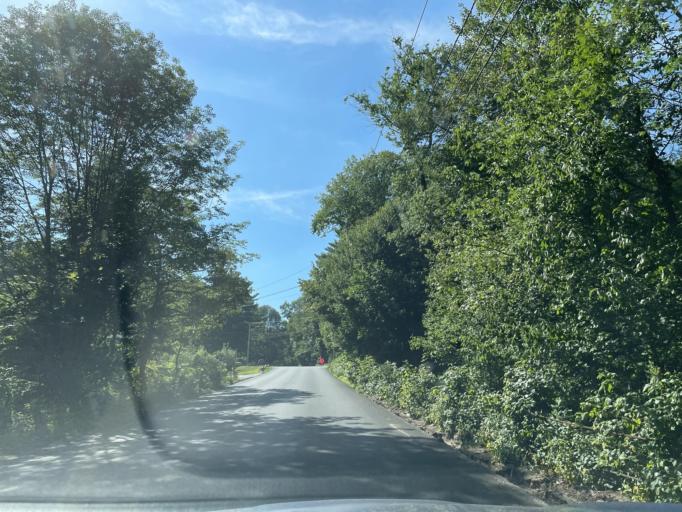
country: US
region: Massachusetts
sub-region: Worcester County
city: Northbridge
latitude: 42.1240
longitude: -71.6104
